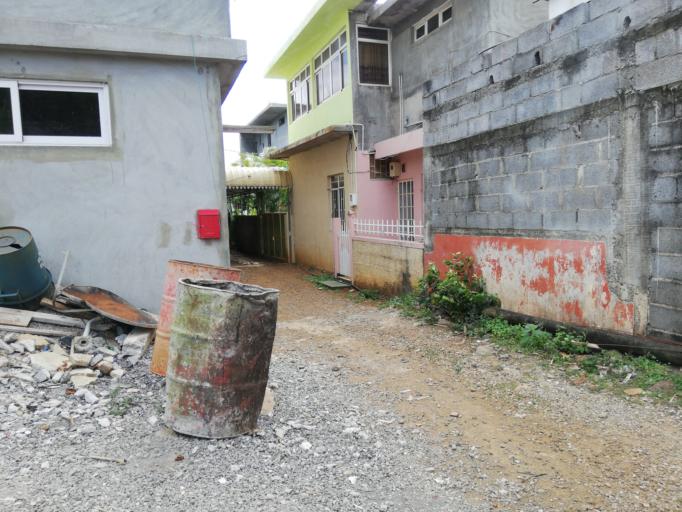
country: MU
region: Black River
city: Petite Riviere
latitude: -20.2163
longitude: 57.4646
